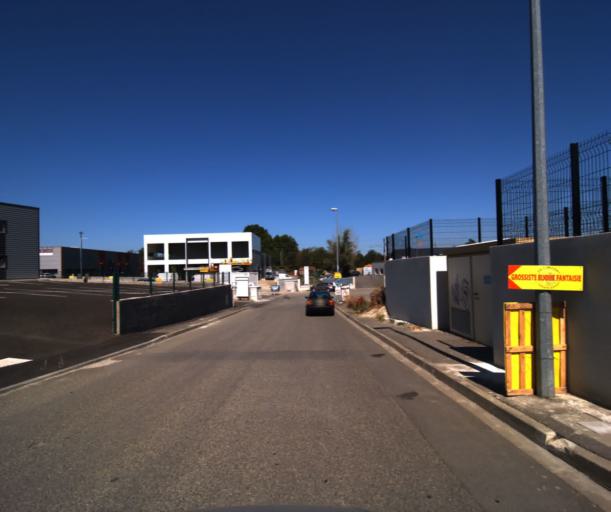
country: FR
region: Midi-Pyrenees
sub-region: Departement de la Haute-Garonne
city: Saubens
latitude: 43.4771
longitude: 1.3323
